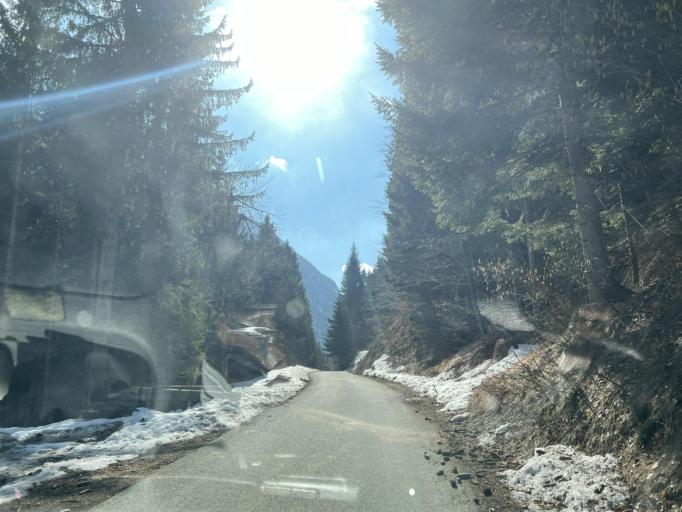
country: AT
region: Carinthia
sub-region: Politischer Bezirk Spittal an der Drau
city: Oberdrauburg
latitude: 46.6533
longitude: 12.9750
